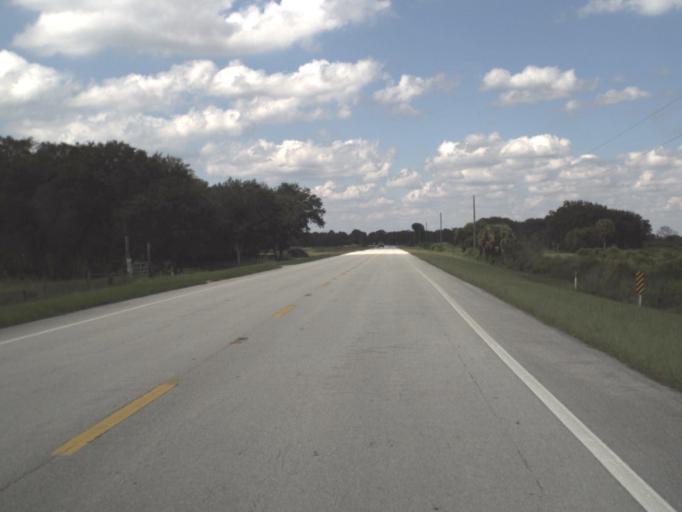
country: US
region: Florida
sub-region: Highlands County
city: Lake Placid
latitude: 27.3782
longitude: -81.1003
